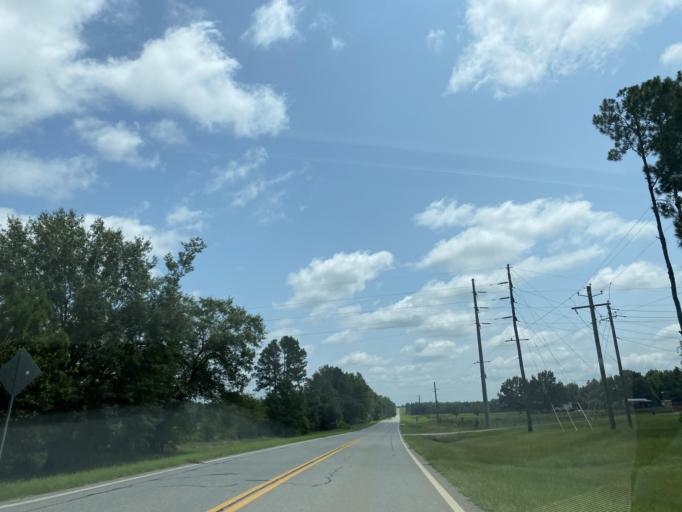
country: US
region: Georgia
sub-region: Wilcox County
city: Abbeville
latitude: 32.0088
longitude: -83.1191
